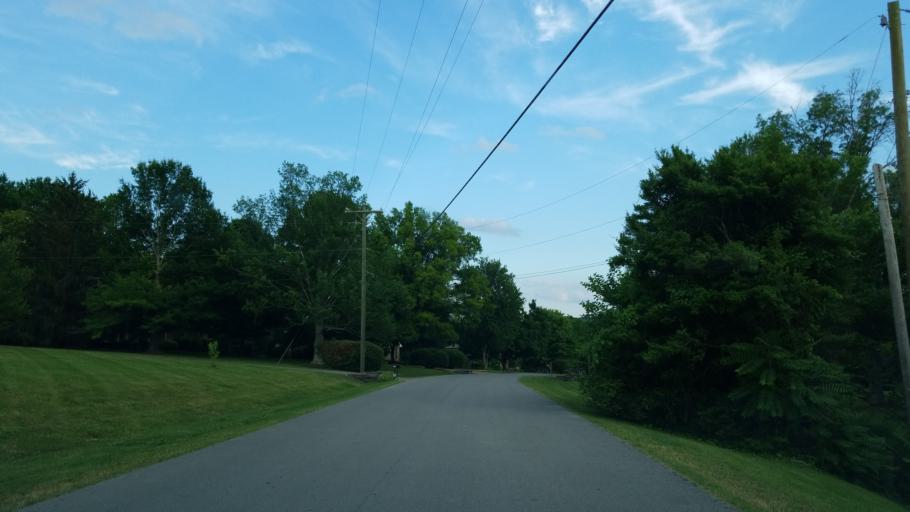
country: US
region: Tennessee
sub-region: Davidson County
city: Forest Hills
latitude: 36.0417
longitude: -86.8419
